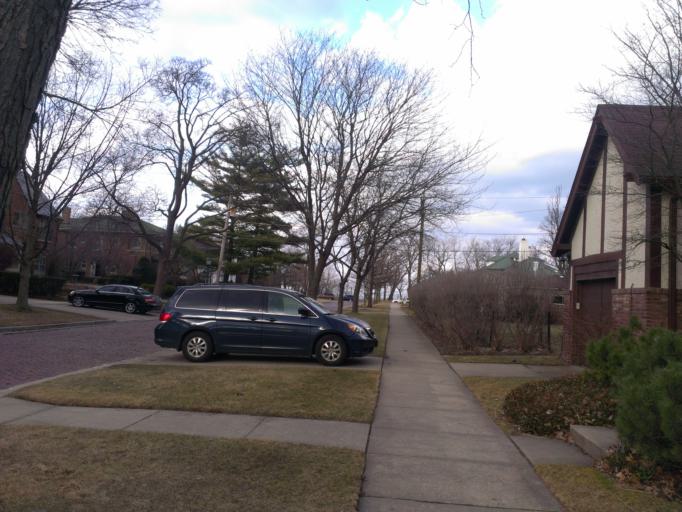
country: US
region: Illinois
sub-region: Cook County
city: Kenilworth
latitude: 42.0804
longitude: -87.6933
